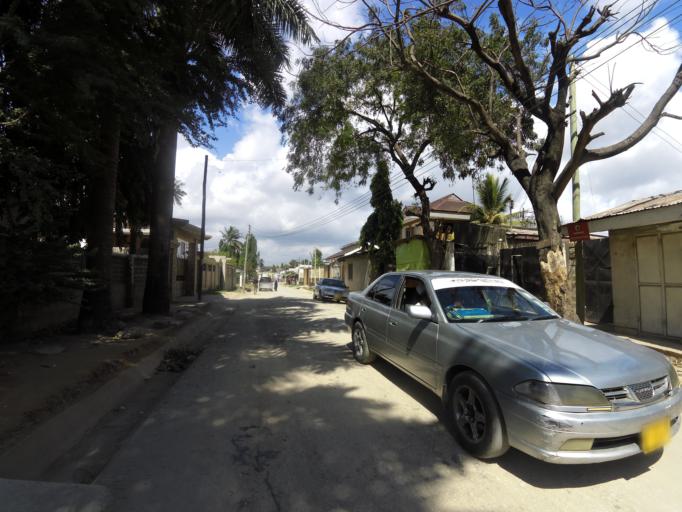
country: TZ
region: Dar es Salaam
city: Magomeni
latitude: -6.7881
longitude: 39.2592
